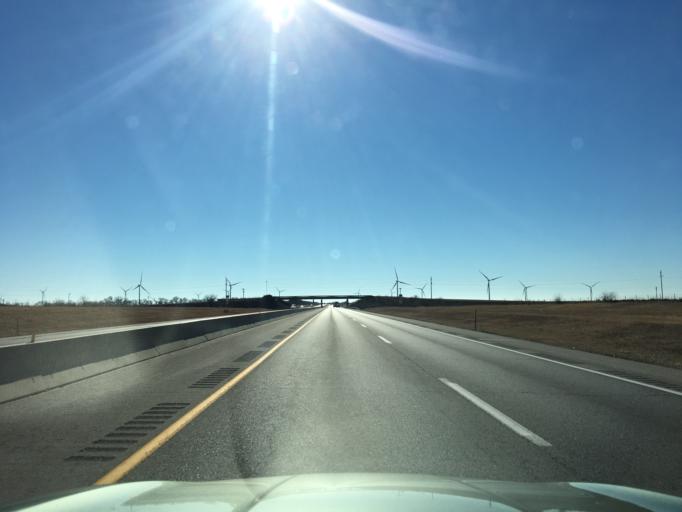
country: US
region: Kansas
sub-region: Sumner County
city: Wellington
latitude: 37.1626
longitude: -97.3395
